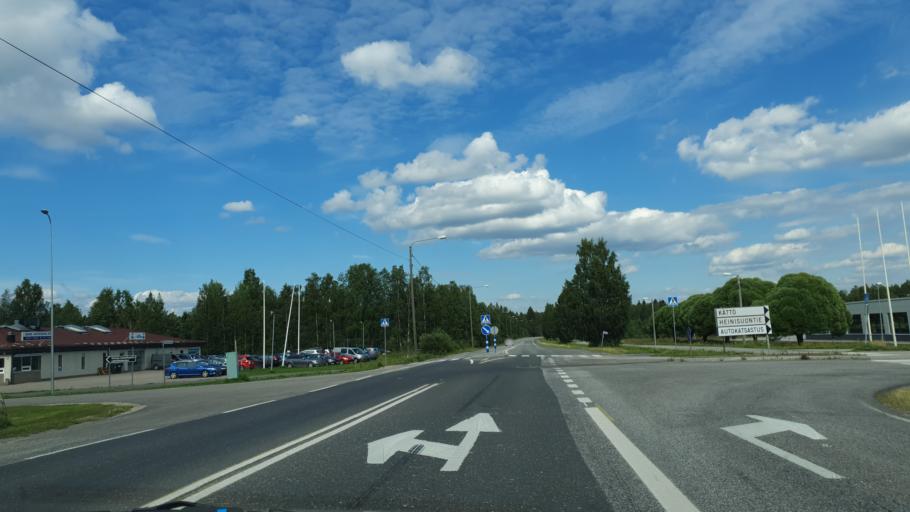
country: FI
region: Kainuu
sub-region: Kajaani
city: Kajaani
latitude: 64.2445
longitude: 27.7610
